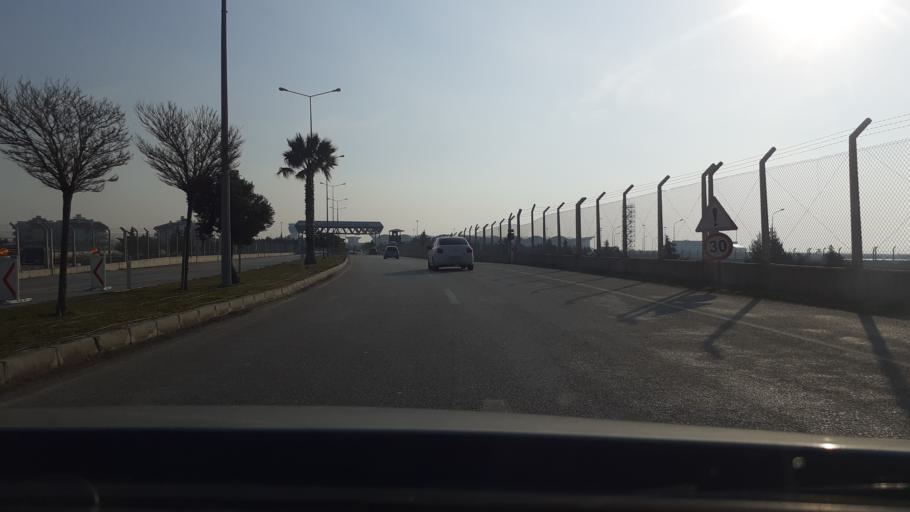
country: TR
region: Hatay
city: Serinyol
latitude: 36.3644
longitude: 36.2736
